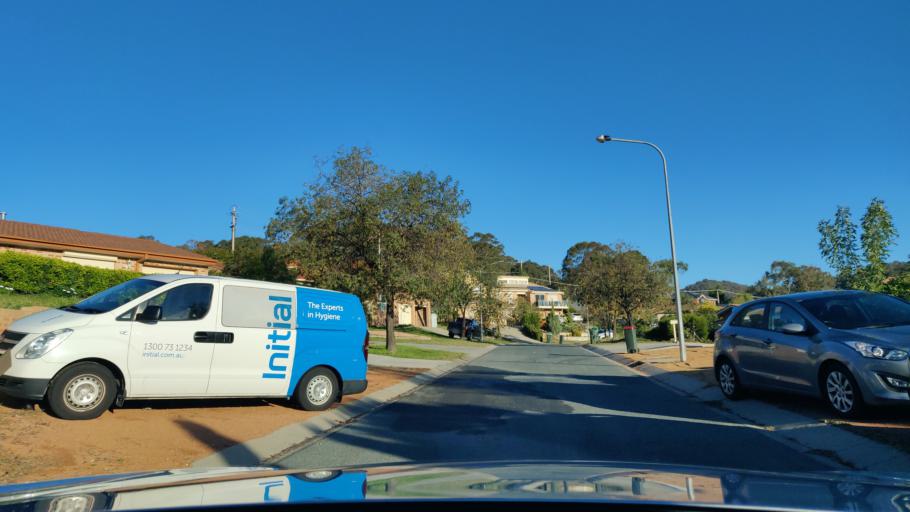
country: AU
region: Australian Capital Territory
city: Macarthur
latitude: -35.4437
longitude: 149.1276
